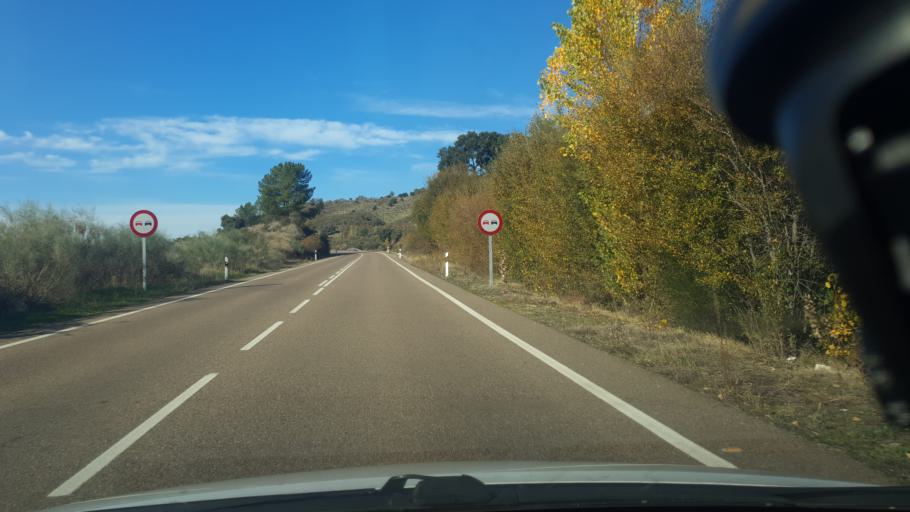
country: ES
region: Castille and Leon
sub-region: Provincia de Avila
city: Poyales del Hoyo
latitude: 40.1586
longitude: -5.1585
